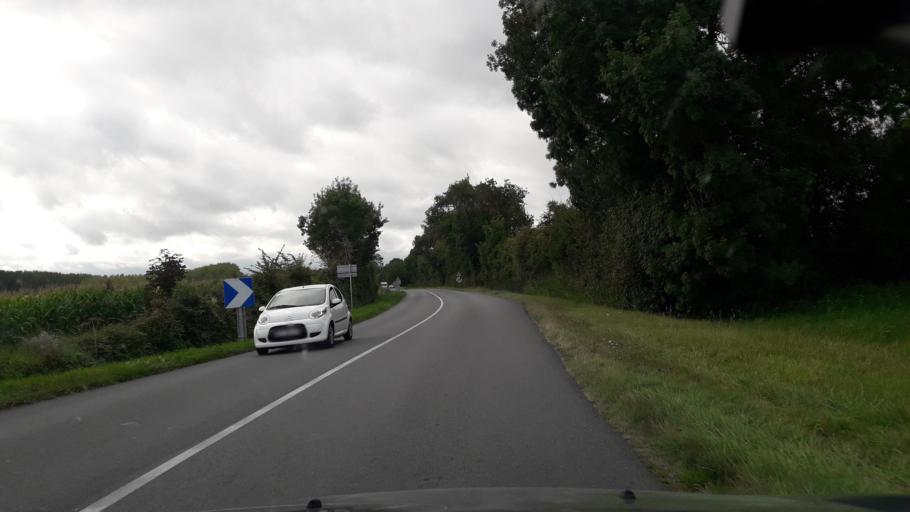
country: FR
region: Poitou-Charentes
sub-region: Departement de la Charente-Maritime
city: Medis
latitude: 45.6751
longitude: -0.9764
